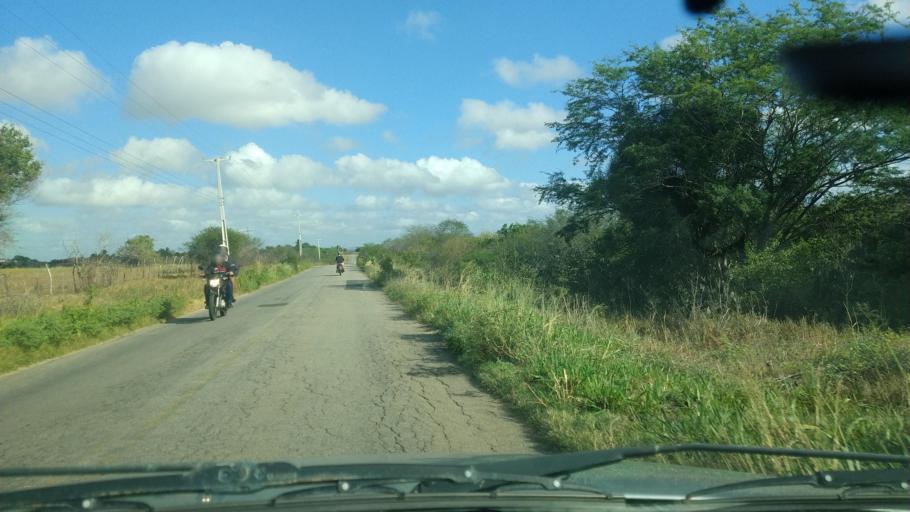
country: BR
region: Rio Grande do Norte
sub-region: Sao Paulo Do Potengi
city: Sao Paulo do Potengi
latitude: -5.9002
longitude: -35.6196
